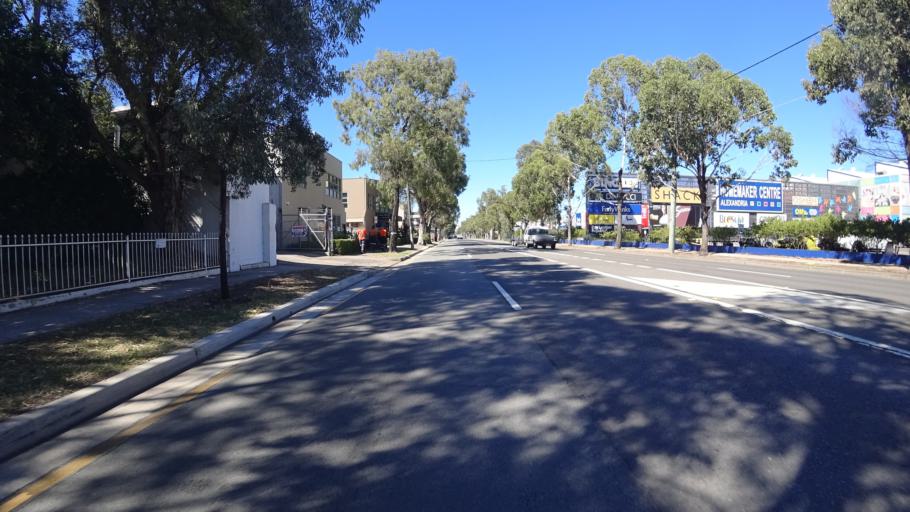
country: AU
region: New South Wales
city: Alexandria
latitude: -33.9136
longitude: 151.1963
